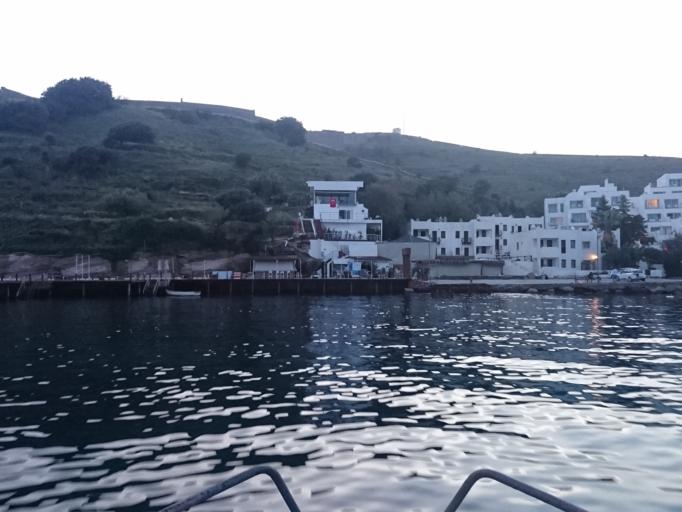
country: TR
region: Mugla
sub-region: Bodrum
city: Bodrum
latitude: 37.0273
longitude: 27.4178
